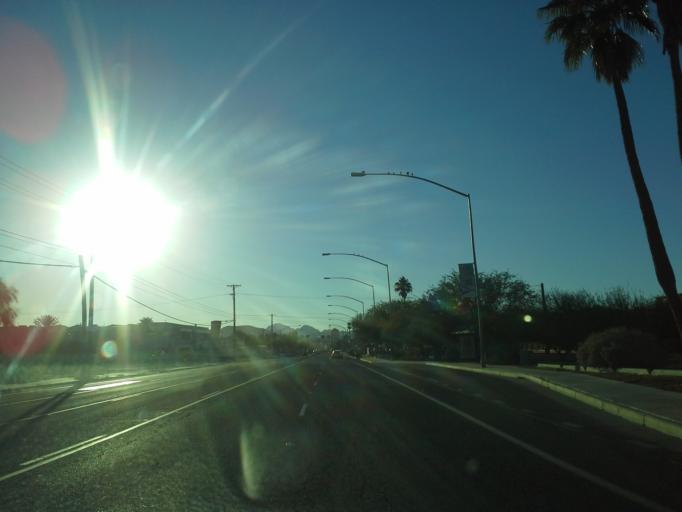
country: US
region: Arizona
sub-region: Pima County
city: Tucson
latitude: 32.2215
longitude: -110.9397
